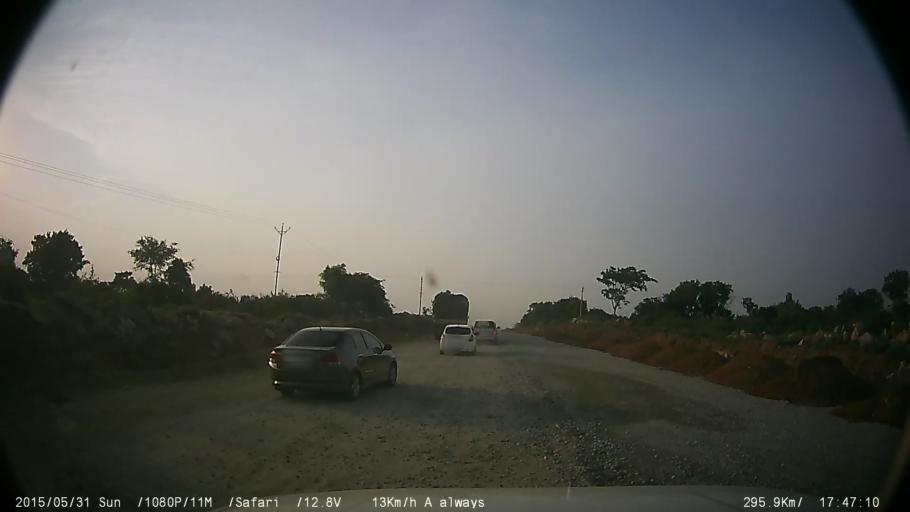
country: IN
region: Karnataka
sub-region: Chamrajnagar
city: Gundlupet
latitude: 11.9612
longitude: 76.6705
